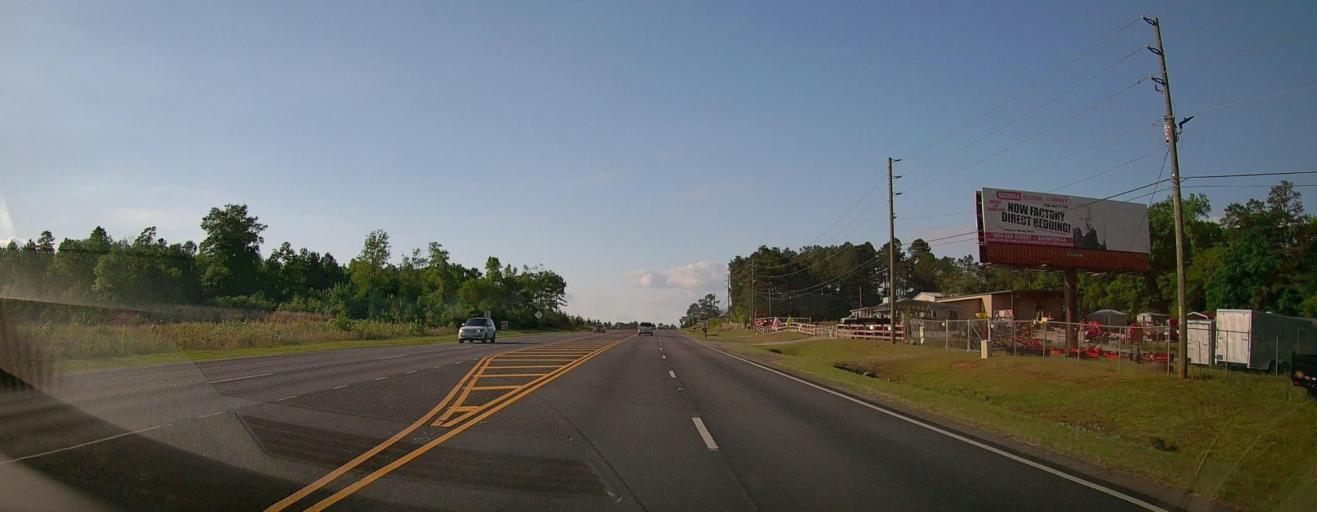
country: US
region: Georgia
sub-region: Baldwin County
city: Milledgeville
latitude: 33.1669
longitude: -83.2803
